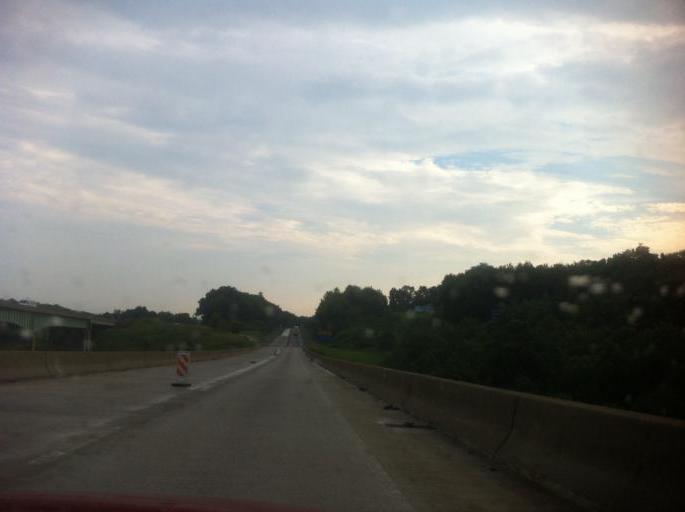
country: US
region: Pennsylvania
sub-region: Clarion County
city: Knox
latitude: 41.1906
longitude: -79.5146
